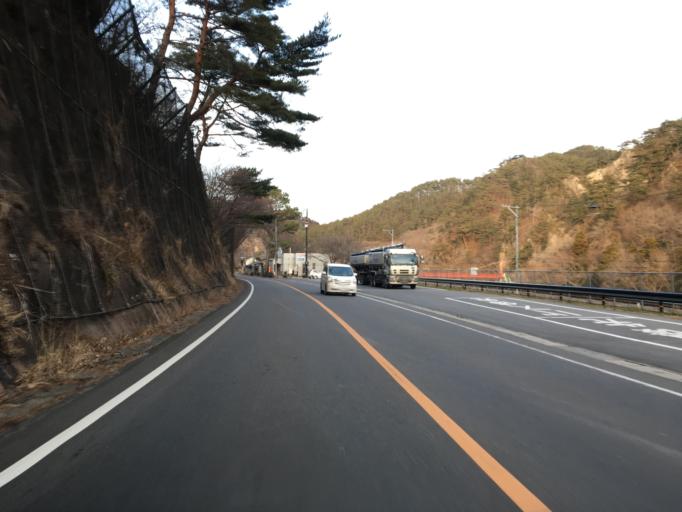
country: JP
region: Ibaraki
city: Daigo
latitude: 36.8486
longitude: 140.3932
